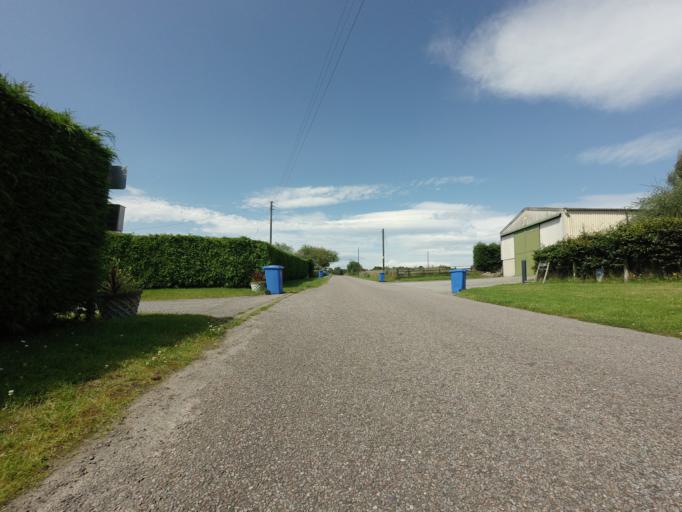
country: GB
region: Scotland
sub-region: Highland
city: Inverness
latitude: 57.5112
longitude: -4.2821
